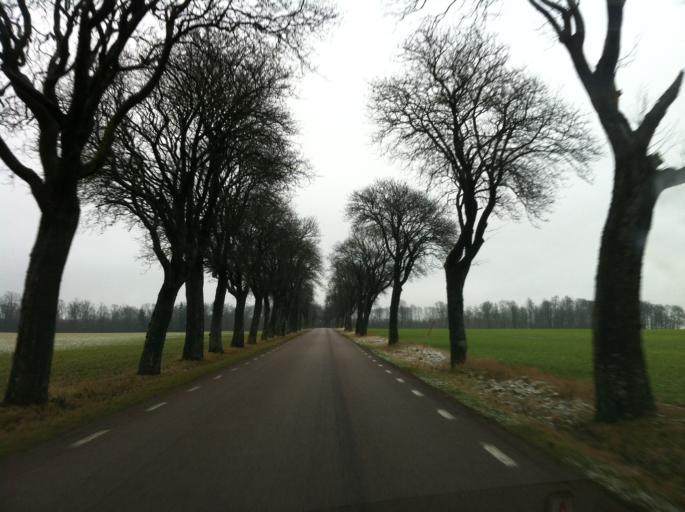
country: SE
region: Skane
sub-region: Landskrona
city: Asmundtorp
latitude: 55.9251
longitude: 12.9984
